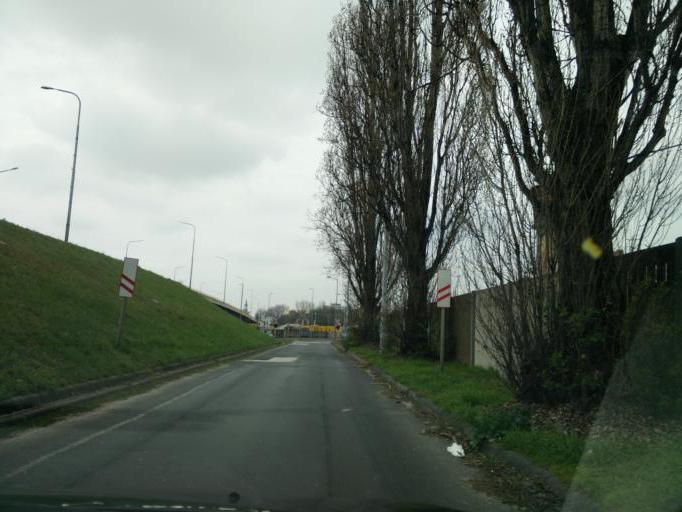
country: HU
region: Gyor-Moson-Sopron
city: Gyor
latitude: 47.6885
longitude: 17.6473
